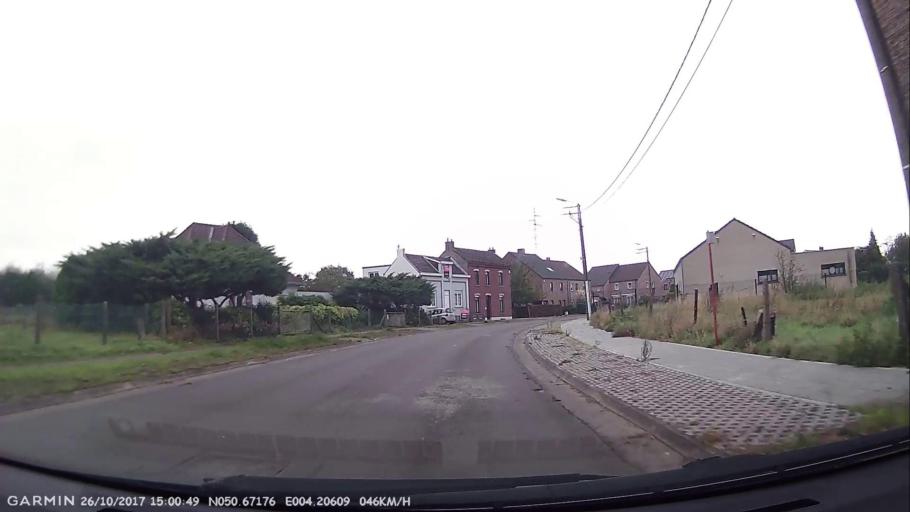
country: BE
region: Wallonia
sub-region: Province du Brabant Wallon
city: Tubize
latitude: 50.6718
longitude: 4.2059
